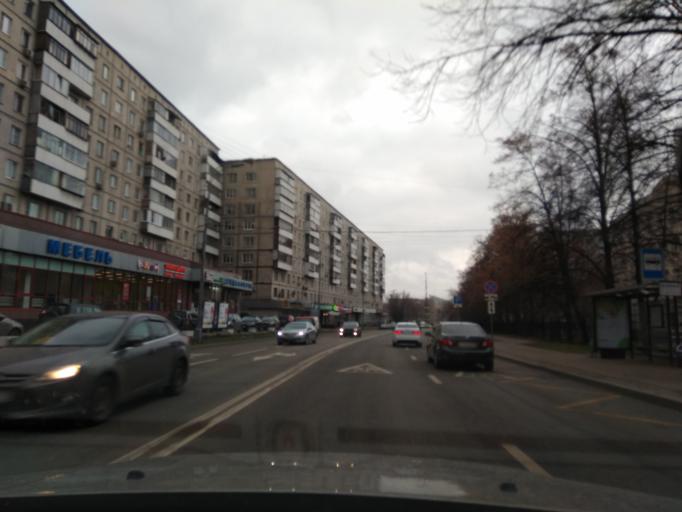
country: RU
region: Moscow
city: Likhobory
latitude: 55.8632
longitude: 37.5668
